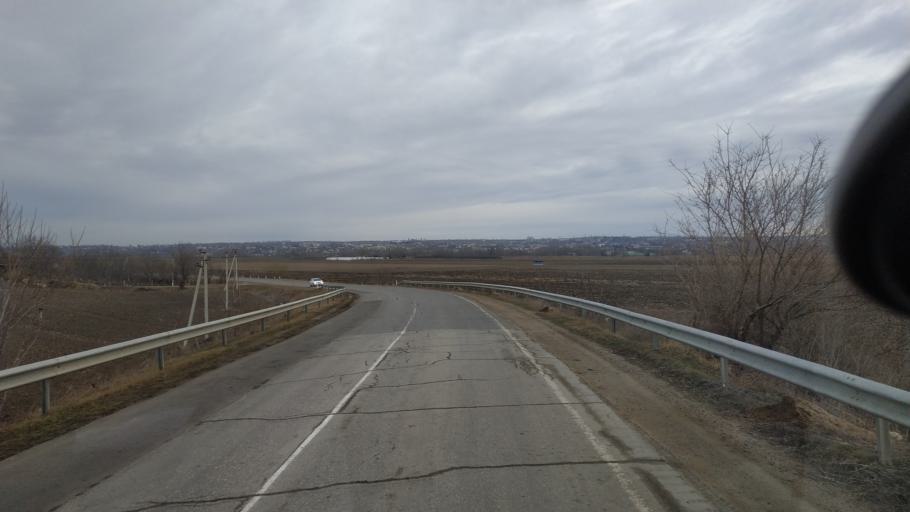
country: MD
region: Telenesti
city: Dubasari
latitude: 47.2531
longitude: 29.1360
